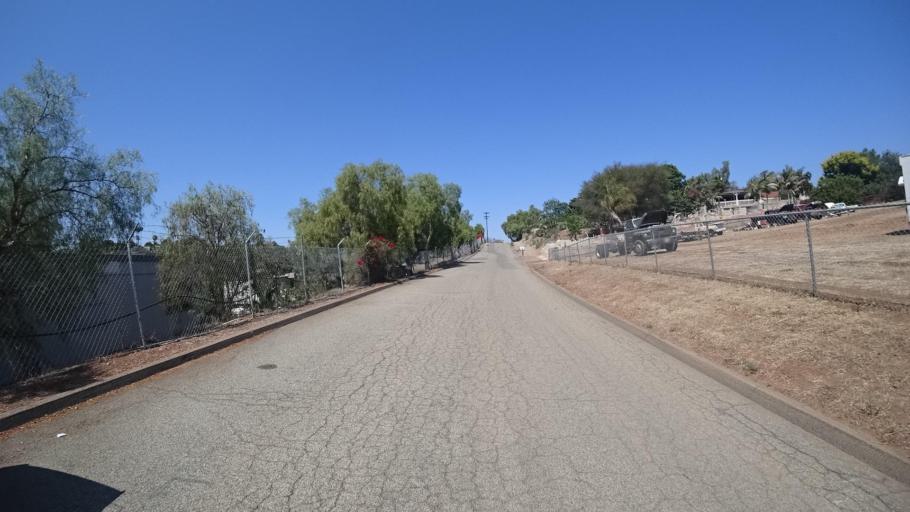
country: US
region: California
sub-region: San Diego County
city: Lake San Marcos
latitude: 33.1658
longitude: -117.2039
